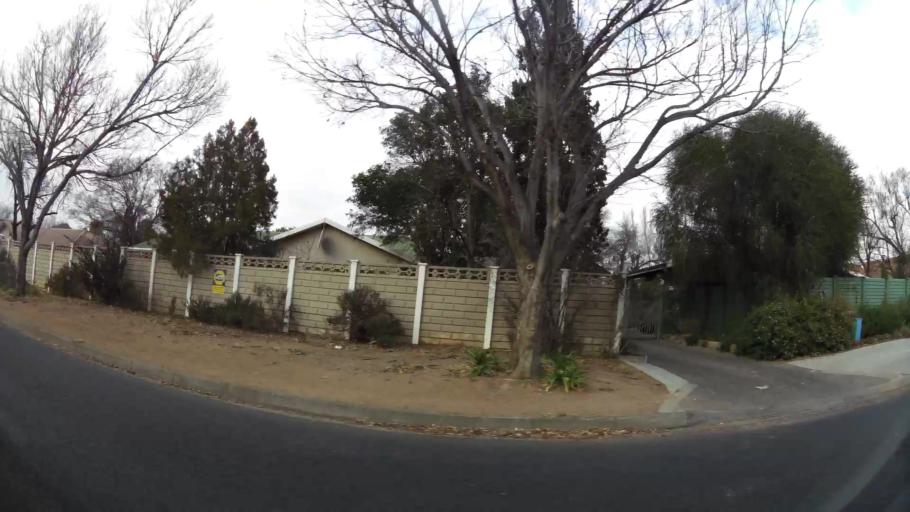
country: ZA
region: Orange Free State
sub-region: Mangaung Metropolitan Municipality
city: Bloemfontein
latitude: -29.1233
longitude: 26.1868
